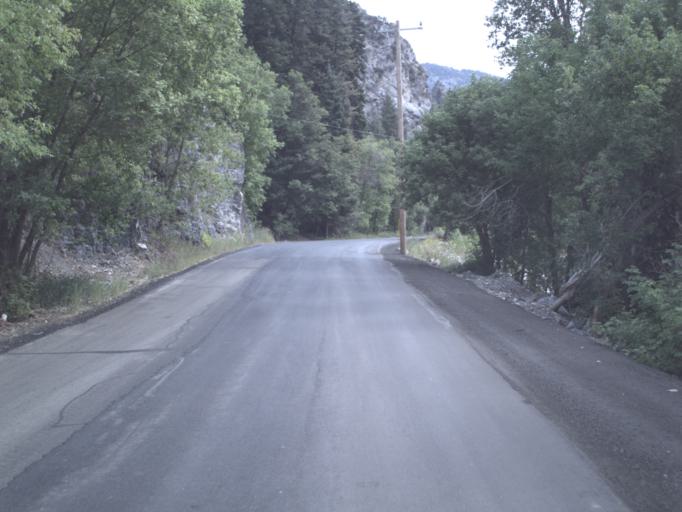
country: US
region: Utah
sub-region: Utah County
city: Cedar Hills
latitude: 40.4471
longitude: -111.6862
